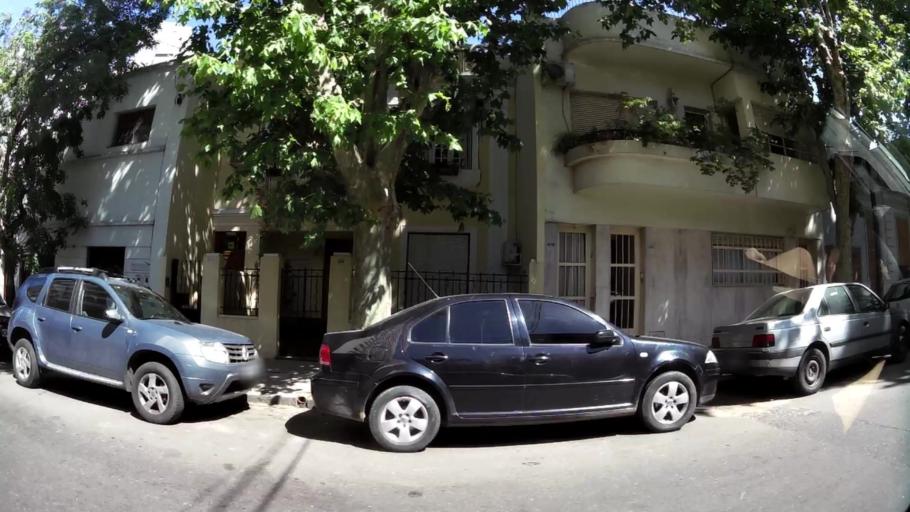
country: AR
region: Buenos Aires F.D.
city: Villa Santa Rita
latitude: -34.6319
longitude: -58.4446
